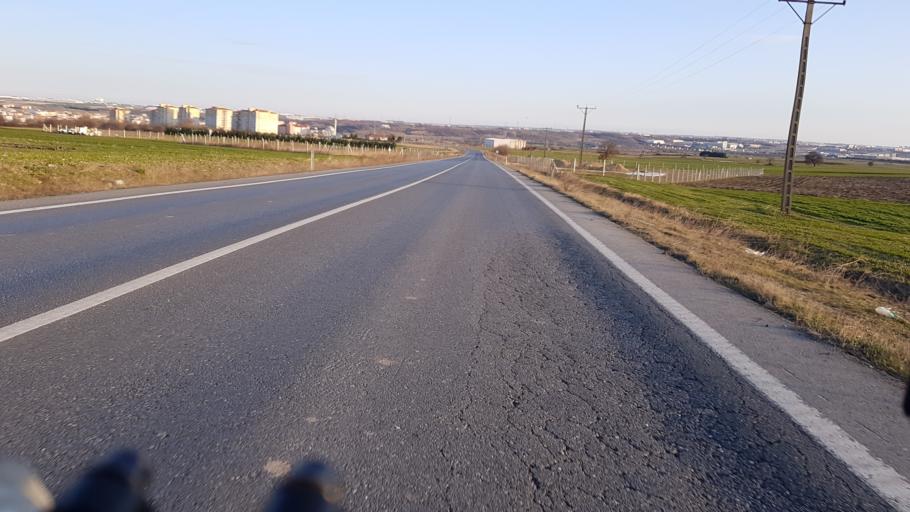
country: TR
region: Tekirdag
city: Velimese
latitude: 41.2590
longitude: 27.8595
